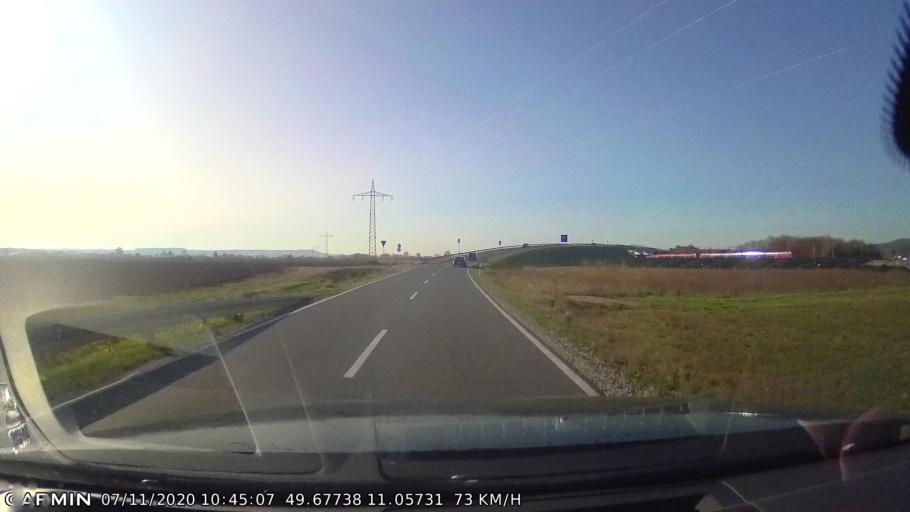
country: DE
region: Bavaria
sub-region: Upper Franconia
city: Poxdorf
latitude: 49.6774
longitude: 11.0571
